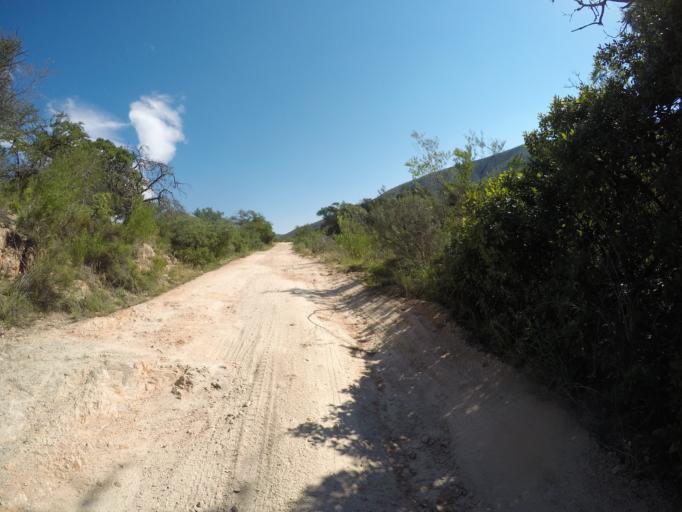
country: ZA
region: Eastern Cape
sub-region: Cacadu District Municipality
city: Kareedouw
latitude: -33.6464
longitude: 24.4618
